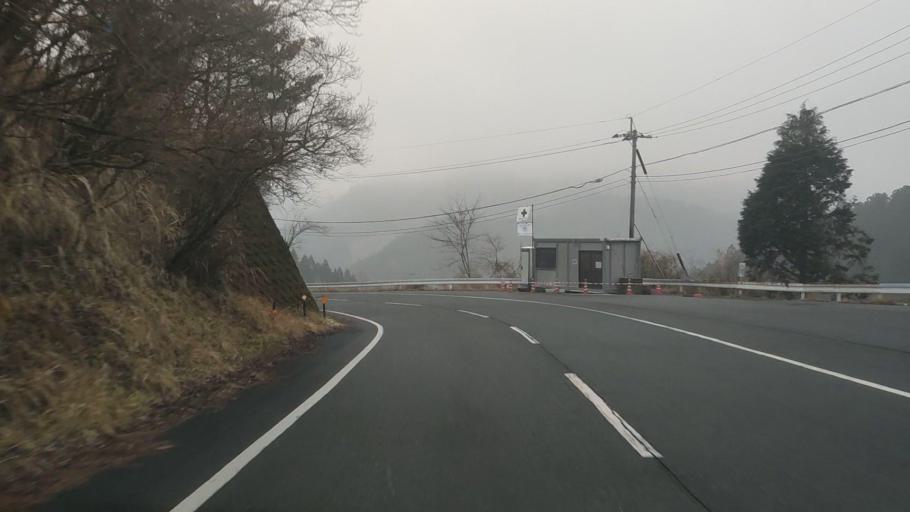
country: JP
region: Kumamoto
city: Matsubase
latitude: 32.5727
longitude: 130.9060
